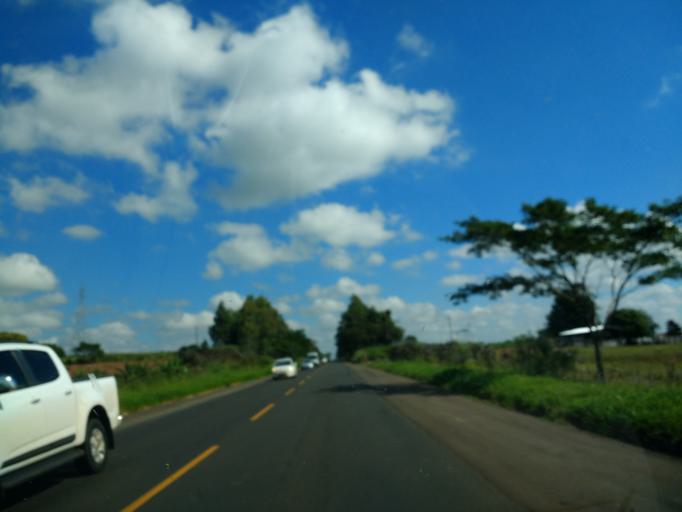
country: BR
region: Parana
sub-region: Umuarama
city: Umuarama
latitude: -23.8565
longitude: -53.3774
